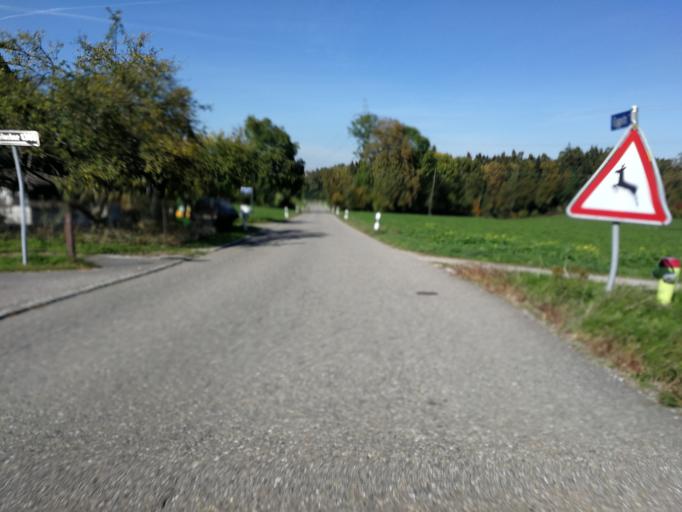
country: CH
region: Zurich
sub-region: Bezirk Uster
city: Hinteregg
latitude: 47.3146
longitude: 8.6763
